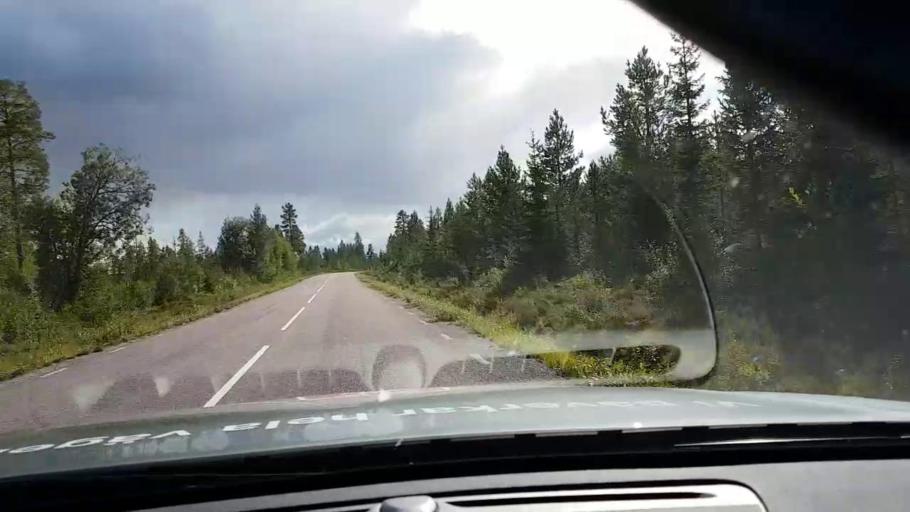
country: SE
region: Vaesterbotten
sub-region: Asele Kommun
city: Asele
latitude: 63.8934
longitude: 17.3499
